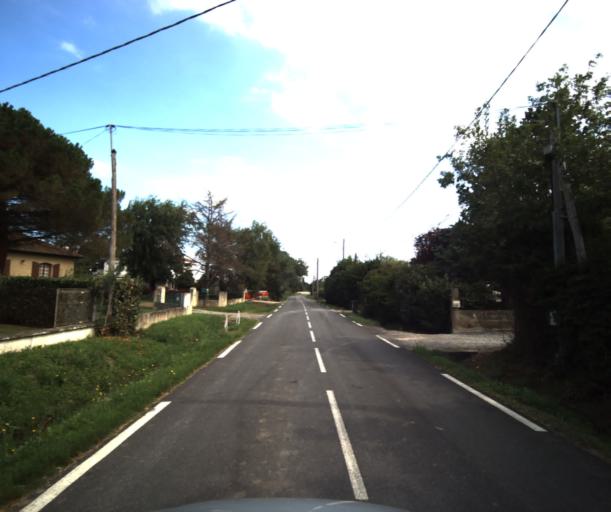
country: FR
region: Midi-Pyrenees
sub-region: Departement de la Haute-Garonne
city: Lacasse
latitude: 43.3986
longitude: 1.2563
